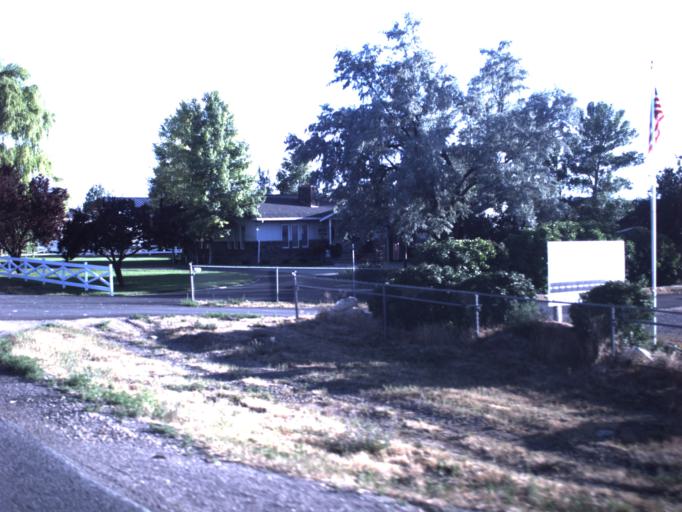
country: US
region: Utah
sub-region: Sanpete County
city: Mount Pleasant
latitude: 39.5655
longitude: -111.4555
